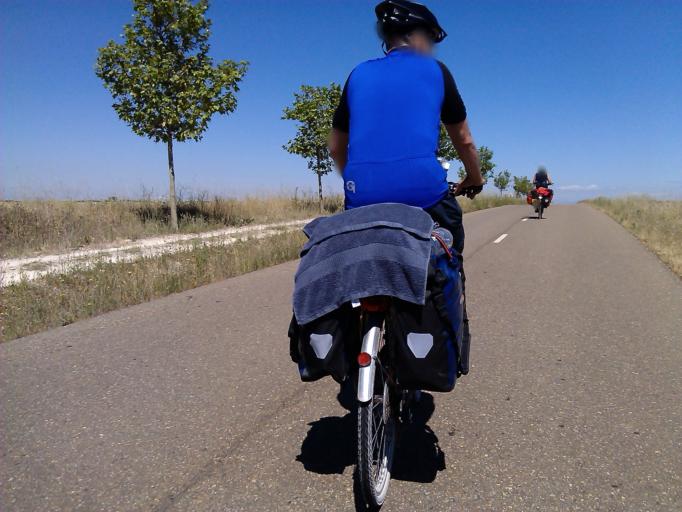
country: ES
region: Castille and Leon
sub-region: Provincia de Leon
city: Villamoratiel de las Matas
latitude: 42.4465
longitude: -5.2653
